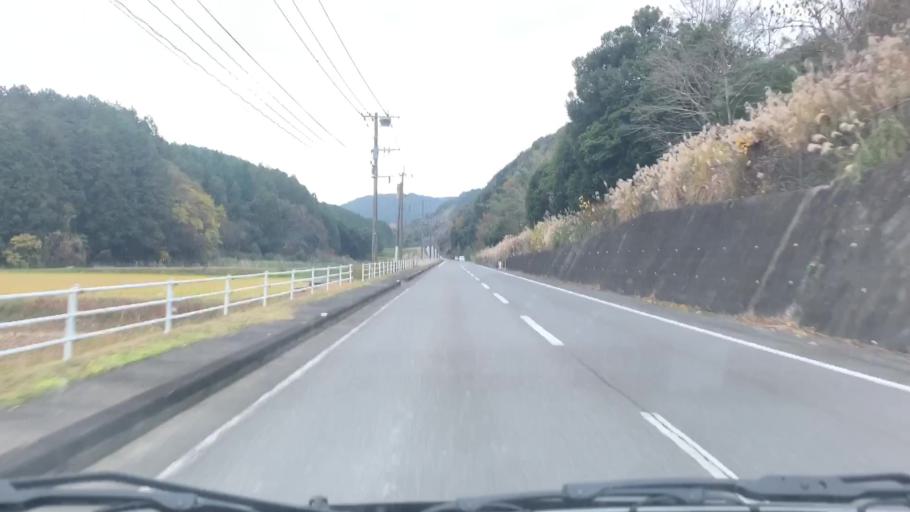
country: JP
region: Saga Prefecture
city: Ureshinomachi-shimojuku
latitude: 33.1201
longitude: 129.9786
